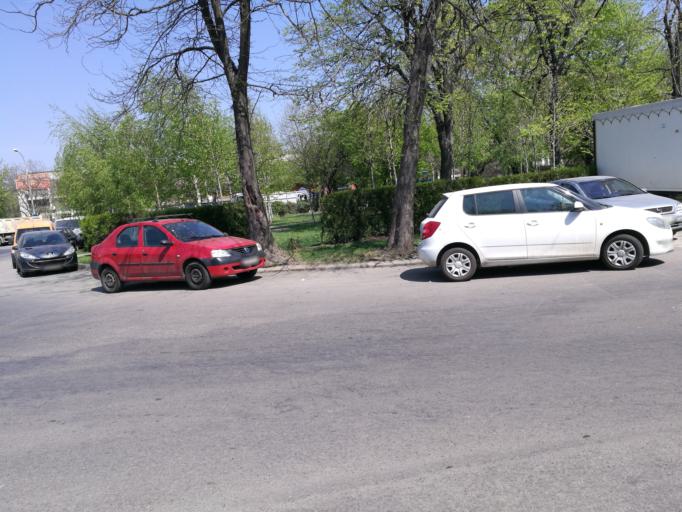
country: RO
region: Ilfov
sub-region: Comuna Popesti-Leordeni
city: Popesti-Leordeni
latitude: 44.4055
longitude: 26.1481
